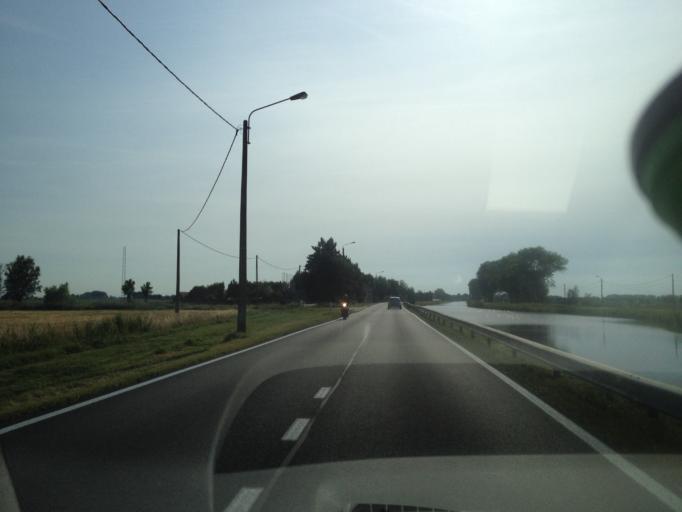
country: BE
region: Flanders
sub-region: Provincie West-Vlaanderen
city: Gistel
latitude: 51.1806
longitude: 2.9573
